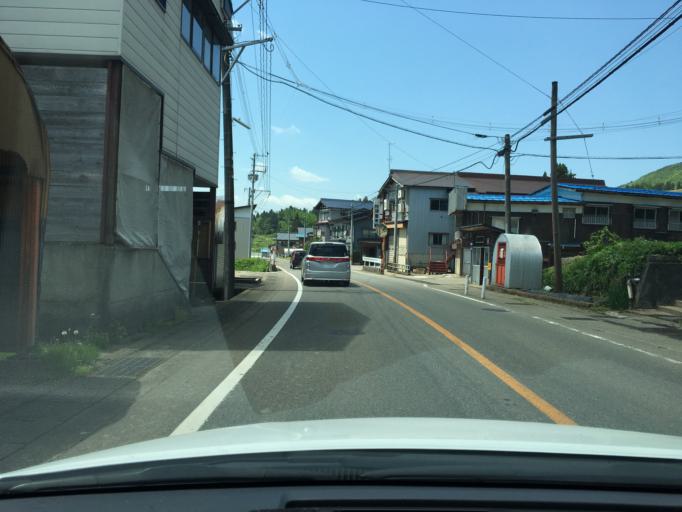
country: JP
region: Niigata
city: Tochio-honcho
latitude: 37.3039
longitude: 139.0000
